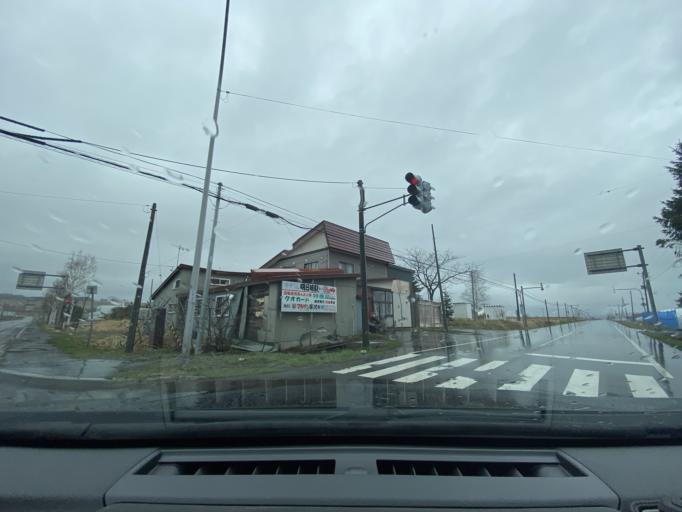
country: JP
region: Hokkaido
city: Fukagawa
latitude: 43.8058
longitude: 141.9055
